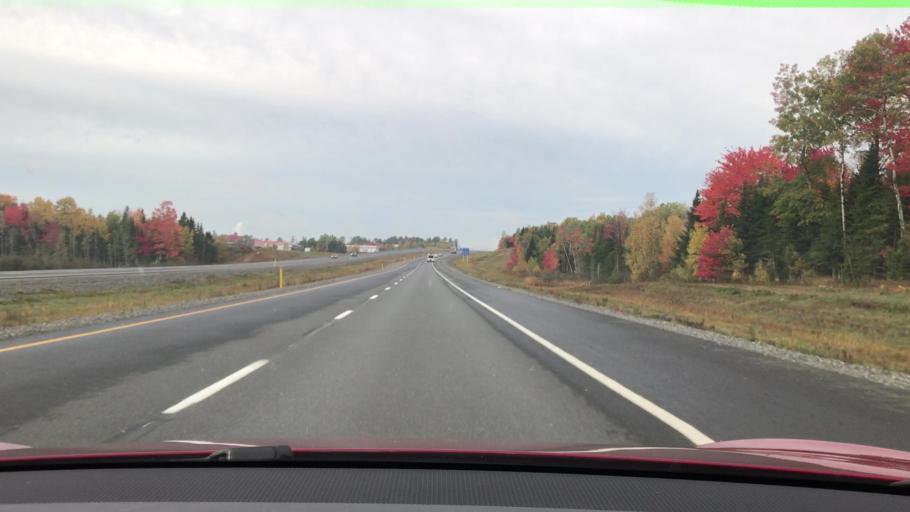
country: US
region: Maine
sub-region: Washington County
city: Calais
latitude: 45.2157
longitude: -67.2450
